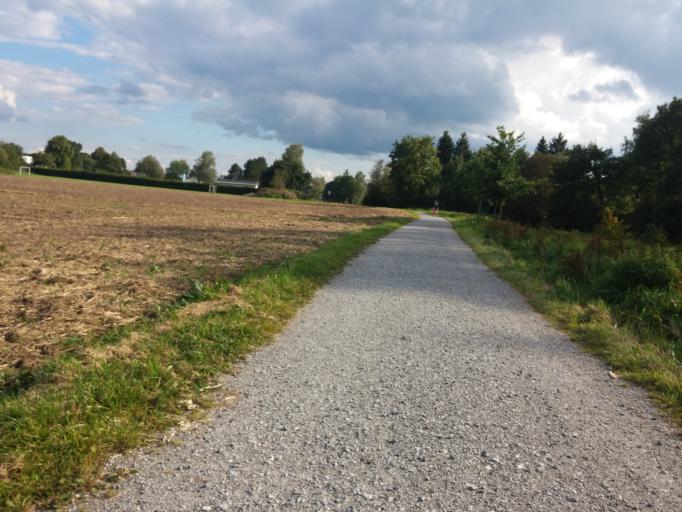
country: DE
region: Bavaria
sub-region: Upper Bavaria
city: Grafing bei Munchen
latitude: 48.0532
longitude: 11.9667
